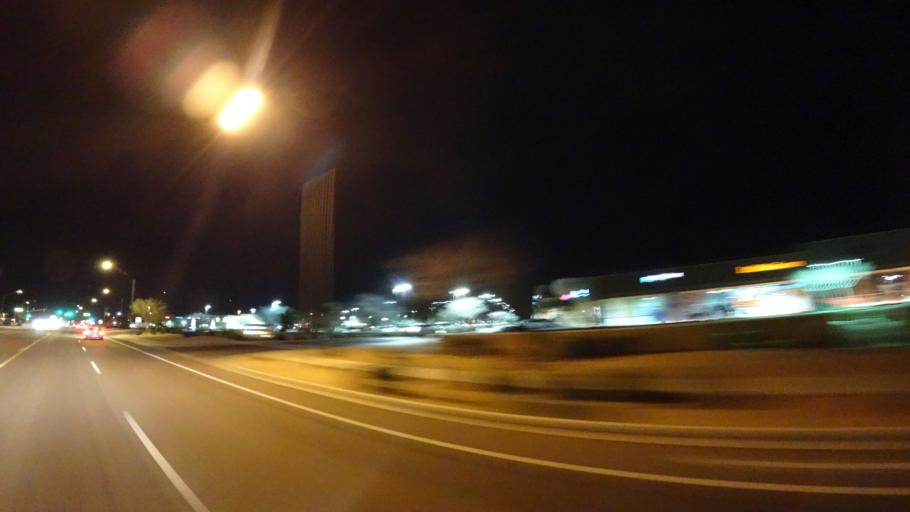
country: US
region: Arizona
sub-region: Maricopa County
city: Gilbert
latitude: 33.3335
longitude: -111.7729
